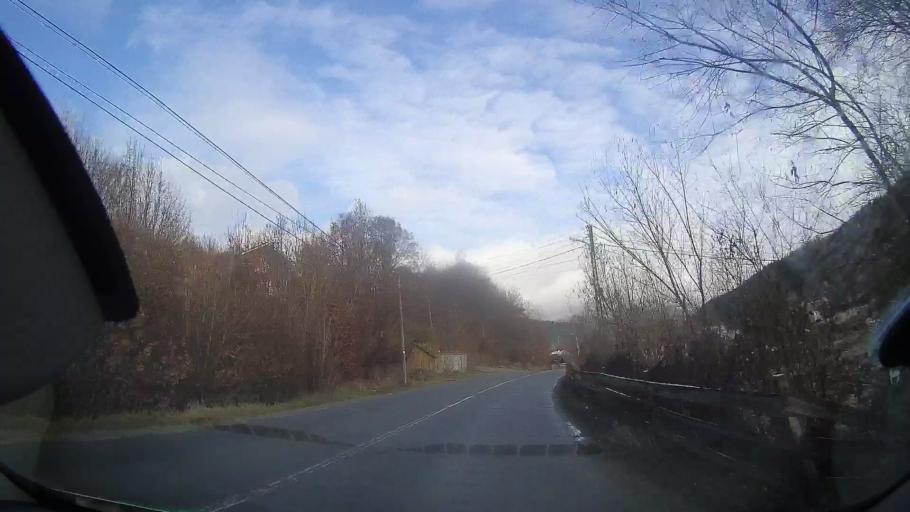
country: RO
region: Alba
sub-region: Comuna Bistra
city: Bistra
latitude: 46.3636
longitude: 23.0807
